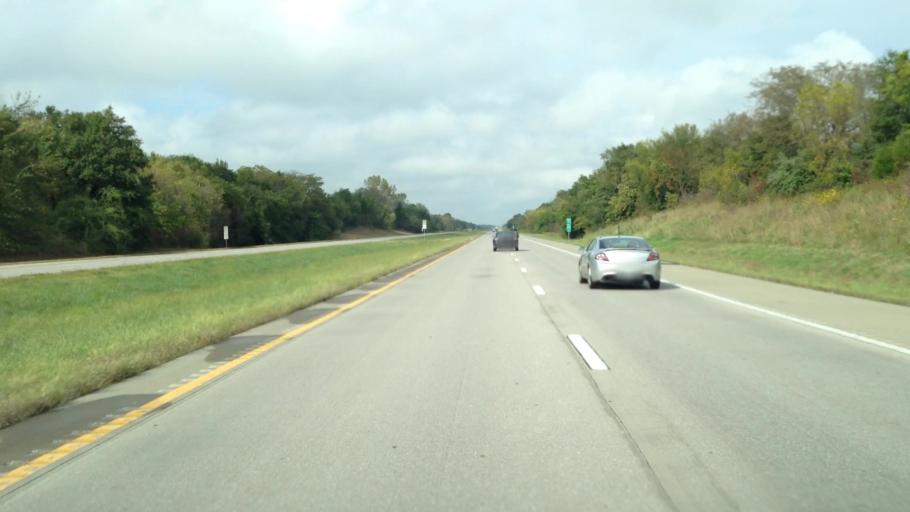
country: US
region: Missouri
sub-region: Clay County
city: Kearney
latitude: 39.3914
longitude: -94.3595
